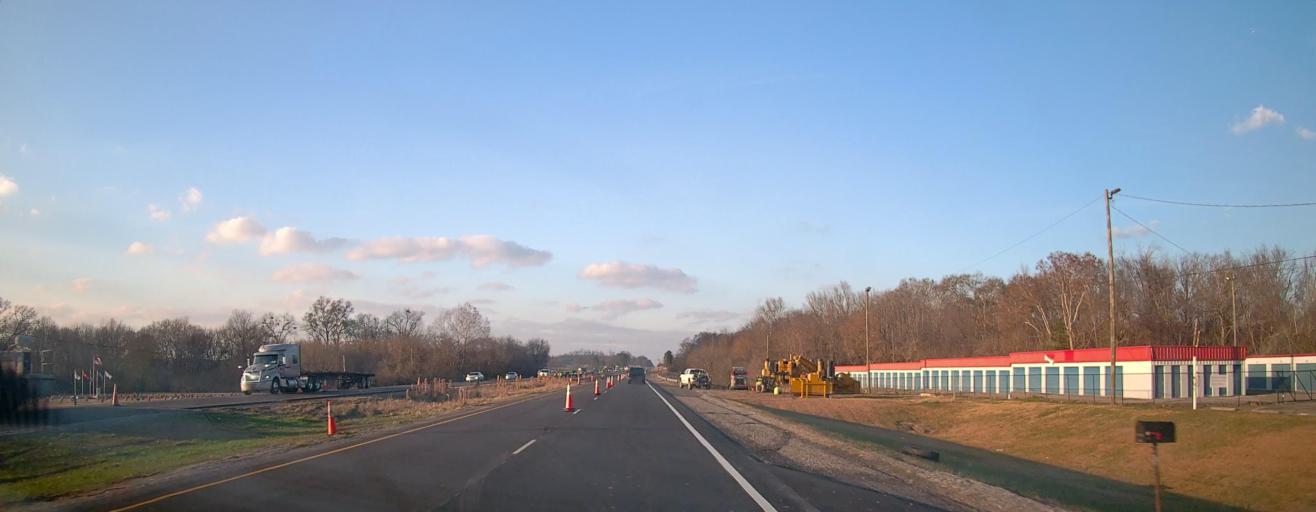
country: US
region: Alabama
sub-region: Calhoun County
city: Alexandria
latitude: 33.7342
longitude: -85.8803
